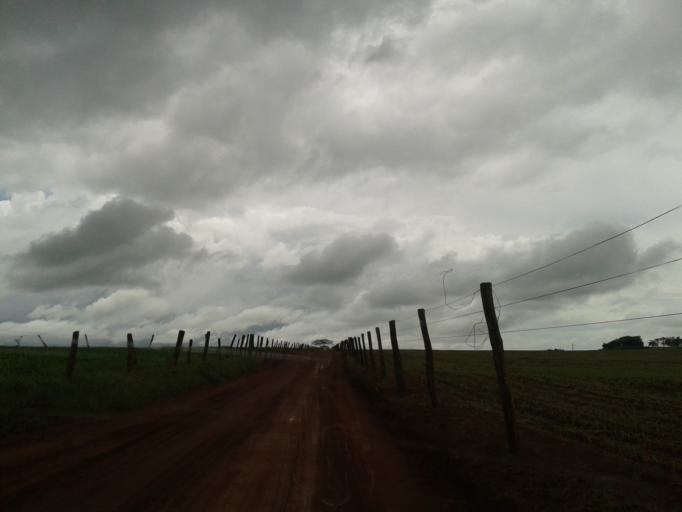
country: BR
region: Minas Gerais
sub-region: Santa Vitoria
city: Santa Vitoria
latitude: -18.6698
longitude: -49.9269
